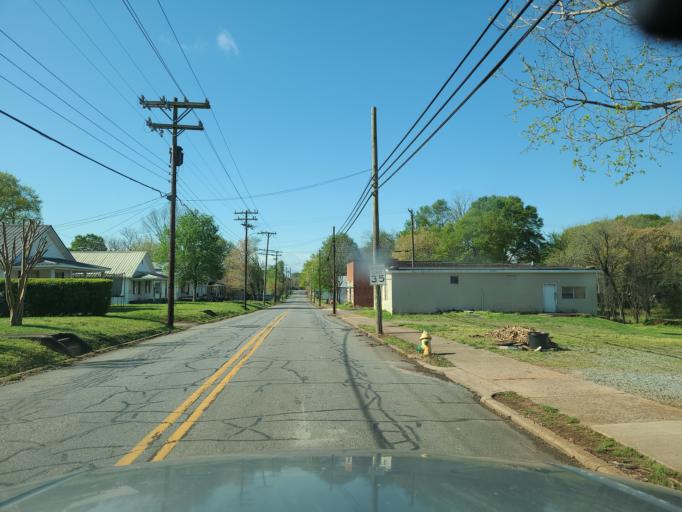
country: US
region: North Carolina
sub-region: Rutherford County
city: Spindale
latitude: 35.3671
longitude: -81.9274
